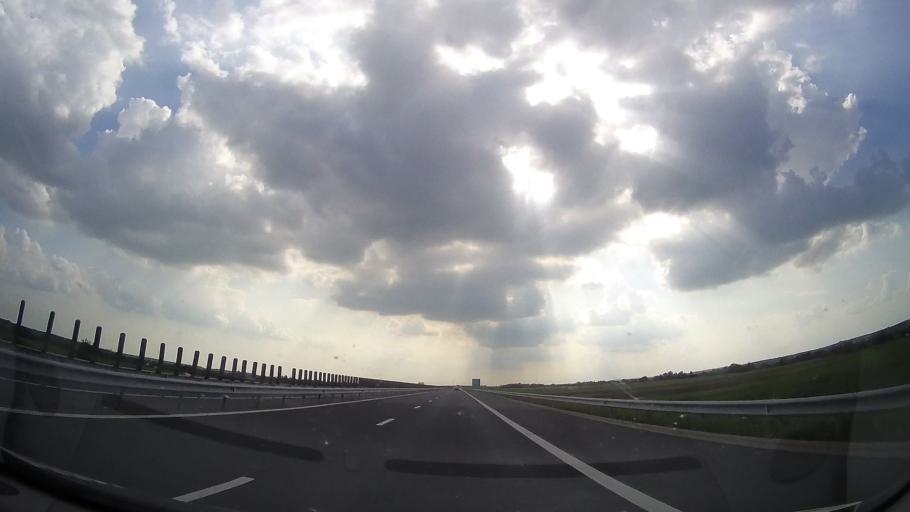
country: RO
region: Timis
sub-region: Comuna Balint
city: Balint
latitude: 45.8038
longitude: 21.8949
